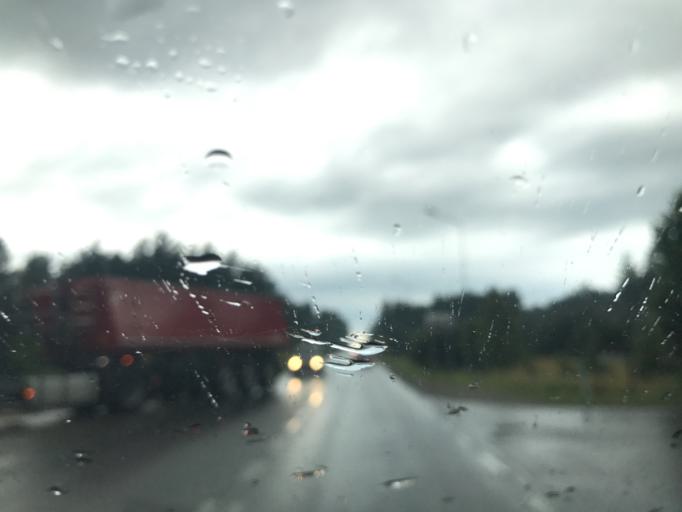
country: PL
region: West Pomeranian Voivodeship
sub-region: Powiat szczecinecki
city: Bialy Bor
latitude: 53.8977
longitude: 16.8278
